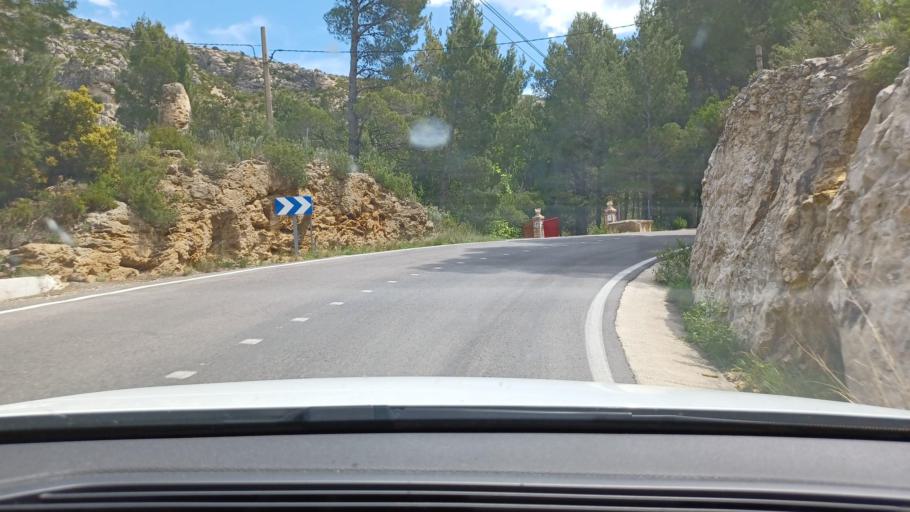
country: ES
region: Valencia
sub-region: Provincia de Castello
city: Rosell
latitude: 40.6609
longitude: 0.2671
